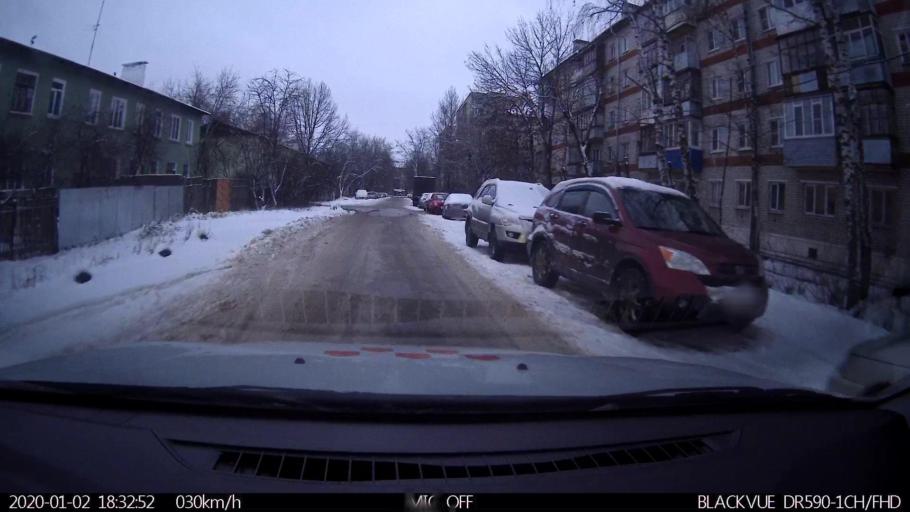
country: RU
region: Nizjnij Novgorod
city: Gorbatovka
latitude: 56.3336
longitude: 43.8367
